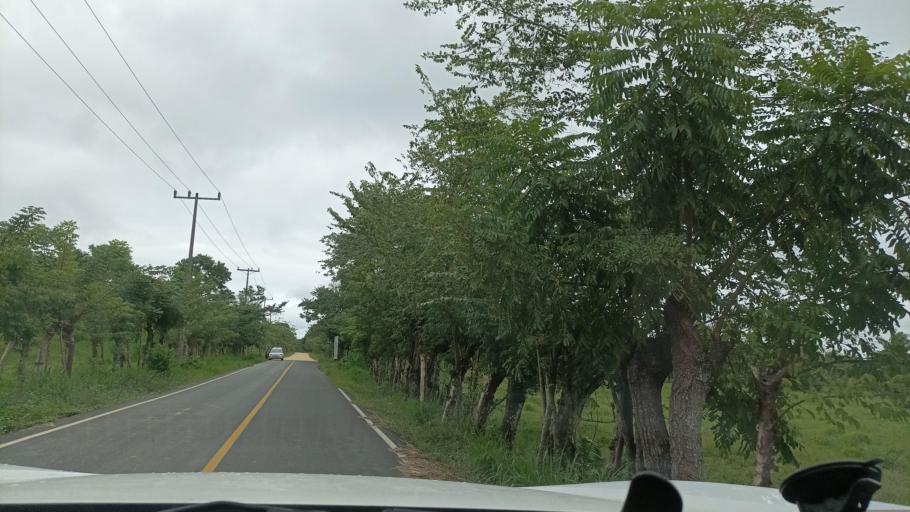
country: MX
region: Veracruz
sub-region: Moloacan
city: Cuichapa
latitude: 17.8136
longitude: -94.3554
